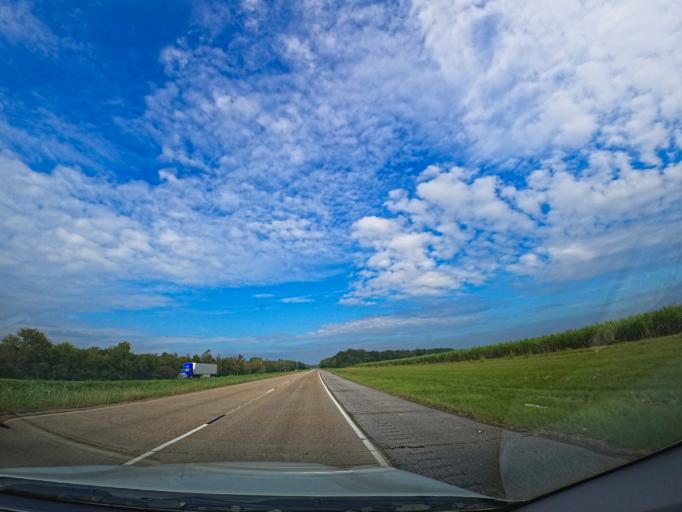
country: US
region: Louisiana
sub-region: Saint Mary Parish
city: Patterson
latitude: 29.7069
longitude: -91.3889
